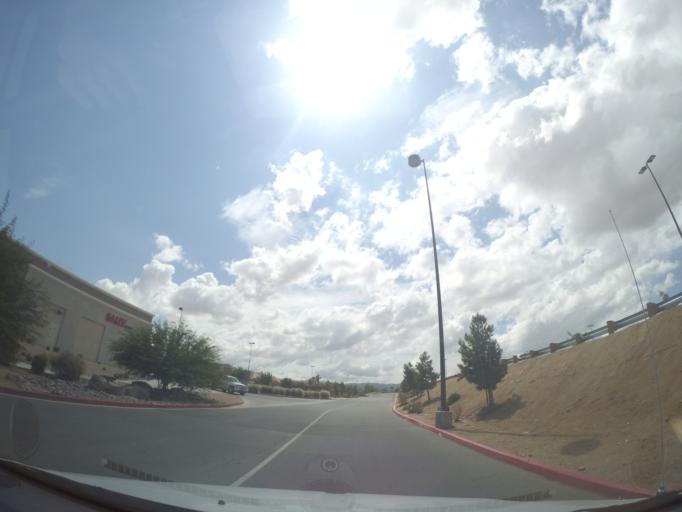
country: US
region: California
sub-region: San Bernardino County
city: Yucca Valley
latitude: 34.1341
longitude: -116.3830
